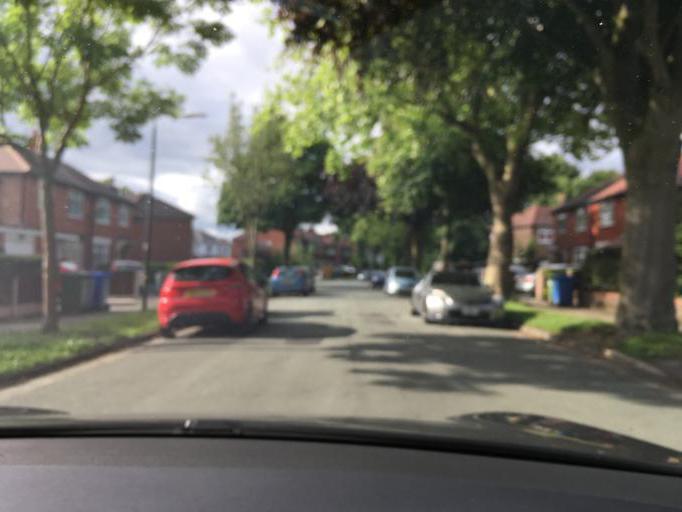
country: GB
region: England
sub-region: Trafford
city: Urmston
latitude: 53.4407
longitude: -2.3662
